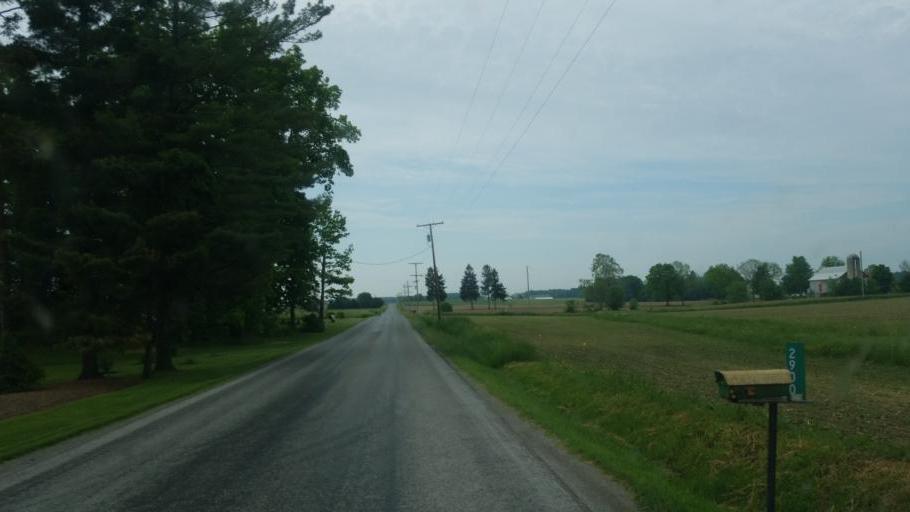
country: US
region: Ohio
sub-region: Wayne County
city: Dalton
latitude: 40.7645
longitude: -81.7550
